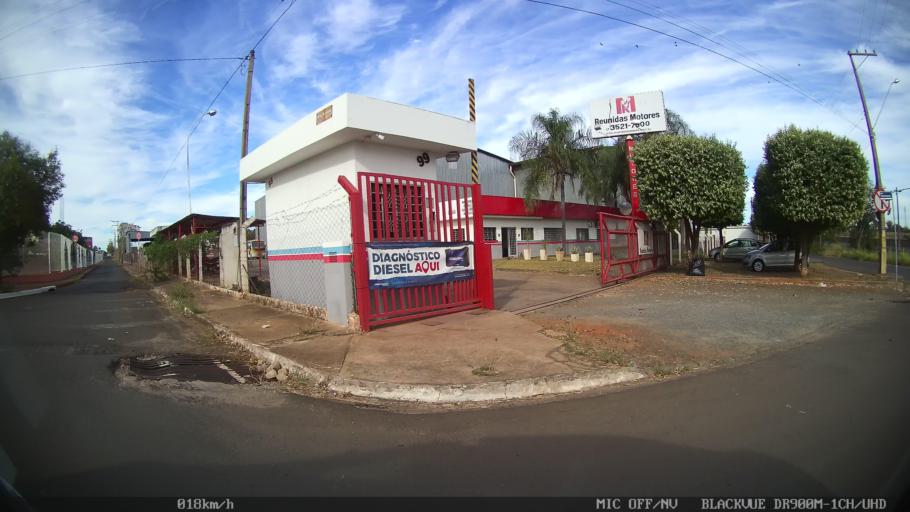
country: BR
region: Sao Paulo
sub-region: Catanduva
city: Catanduva
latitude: -21.1264
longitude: -49.0018
